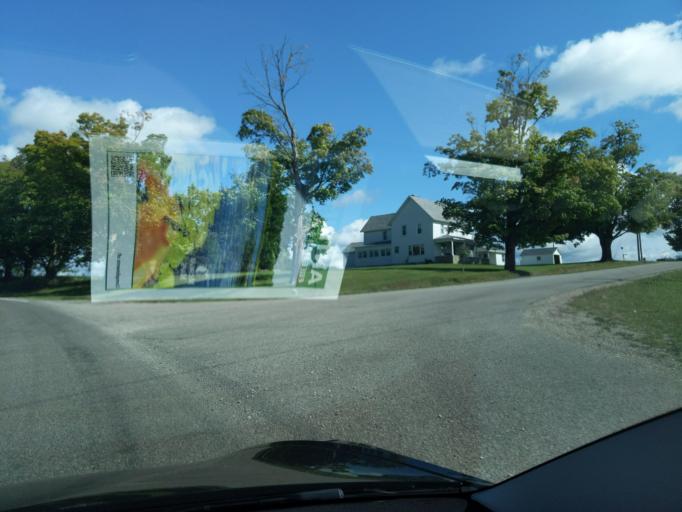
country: US
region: Michigan
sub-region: Antrim County
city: Elk Rapids
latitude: 44.9462
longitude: -85.3530
